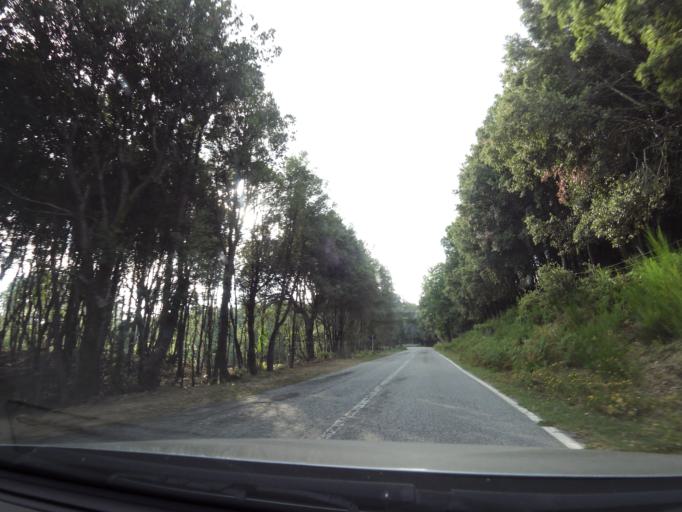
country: IT
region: Calabria
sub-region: Provincia di Vibo-Valentia
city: Nardodipace
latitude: 38.4775
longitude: 16.3924
